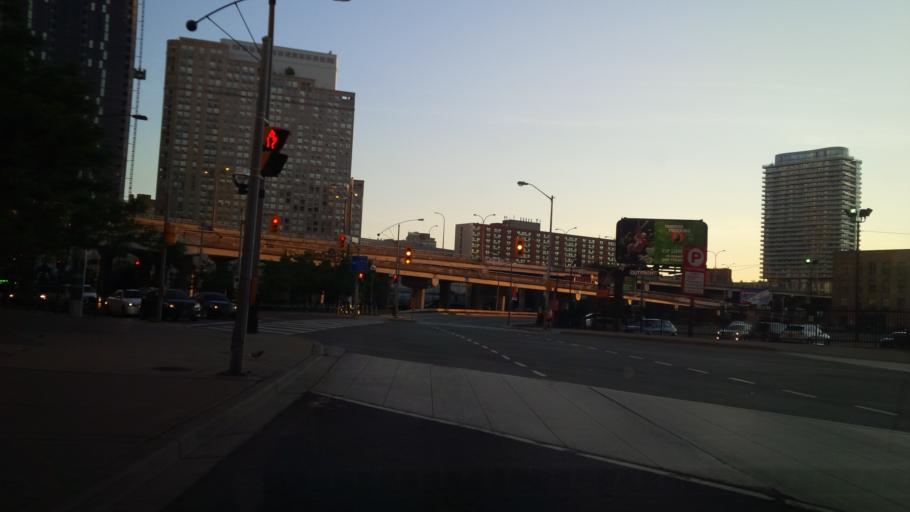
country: CA
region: Ontario
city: Toronto
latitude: 43.6431
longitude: -79.3755
